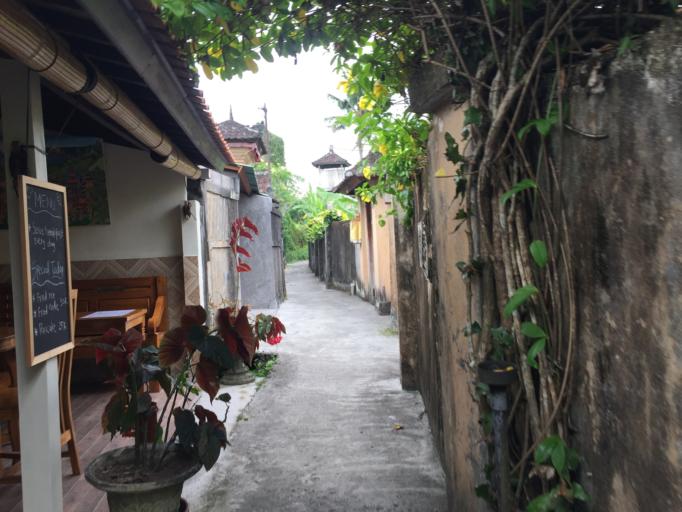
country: ID
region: Bali
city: Banjar Pande
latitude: -8.5042
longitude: 115.2519
